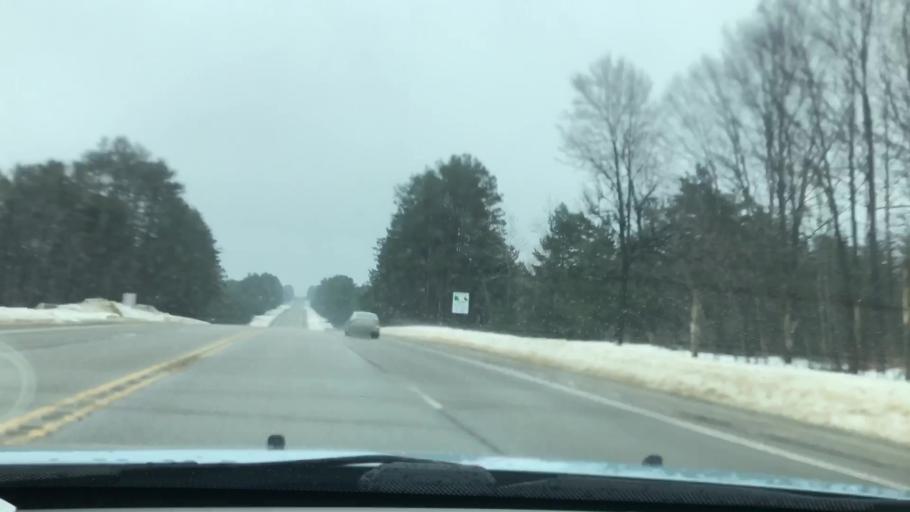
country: US
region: Michigan
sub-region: Otsego County
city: Gaylord
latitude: 45.0620
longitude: -84.8272
